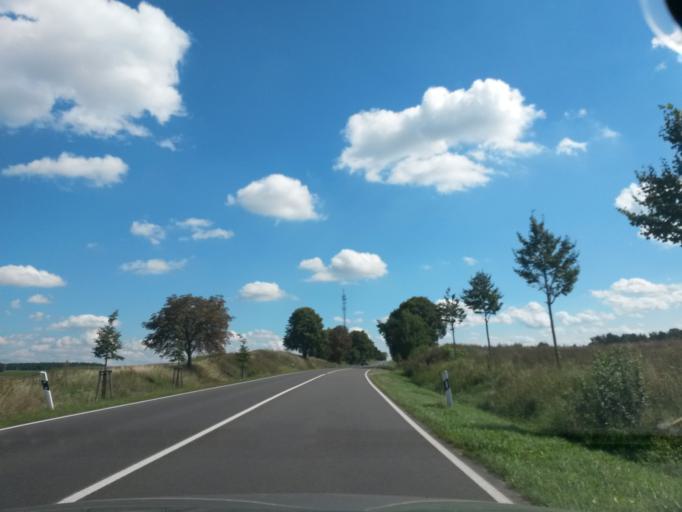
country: DE
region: Brandenburg
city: Schoneberg
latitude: 53.0331
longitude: 14.1333
